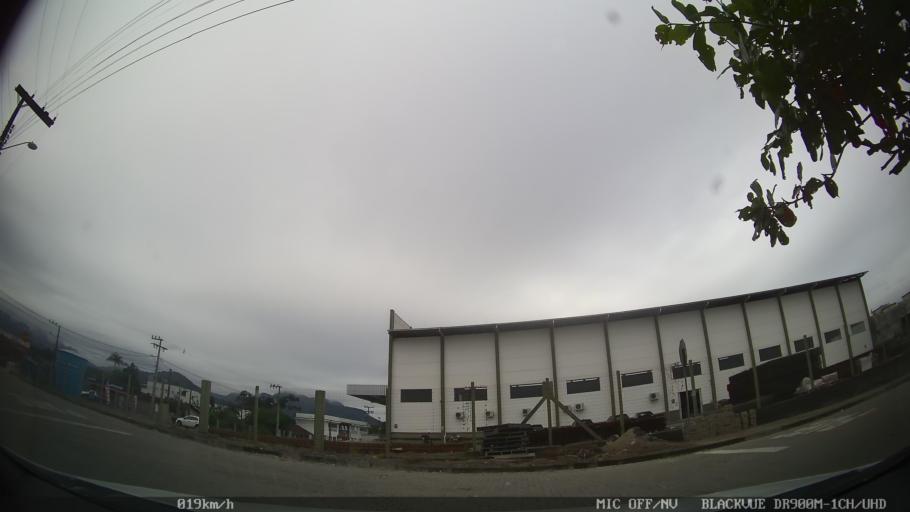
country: BR
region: Santa Catarina
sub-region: Joinville
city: Joinville
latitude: -26.2882
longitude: -48.9094
